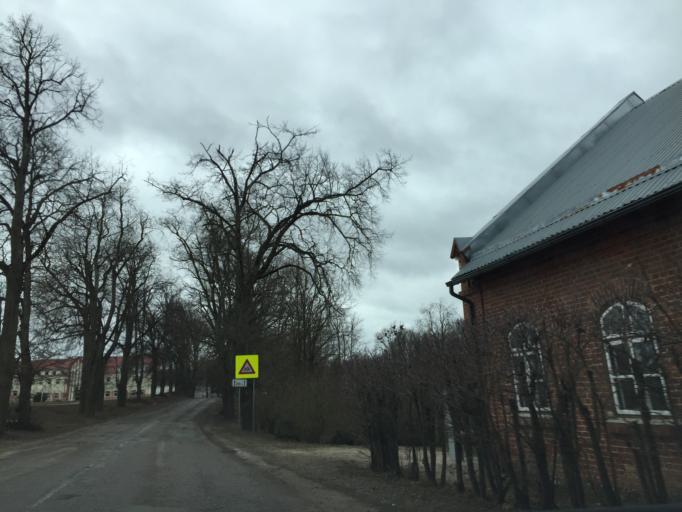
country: LV
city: Tervete
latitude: 56.5288
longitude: 23.5102
